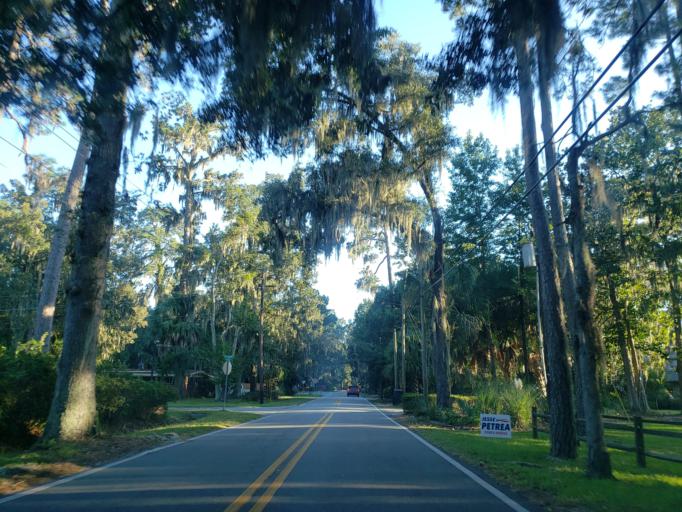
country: US
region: Georgia
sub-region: Chatham County
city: Isle of Hope
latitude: 31.9903
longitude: -81.0553
